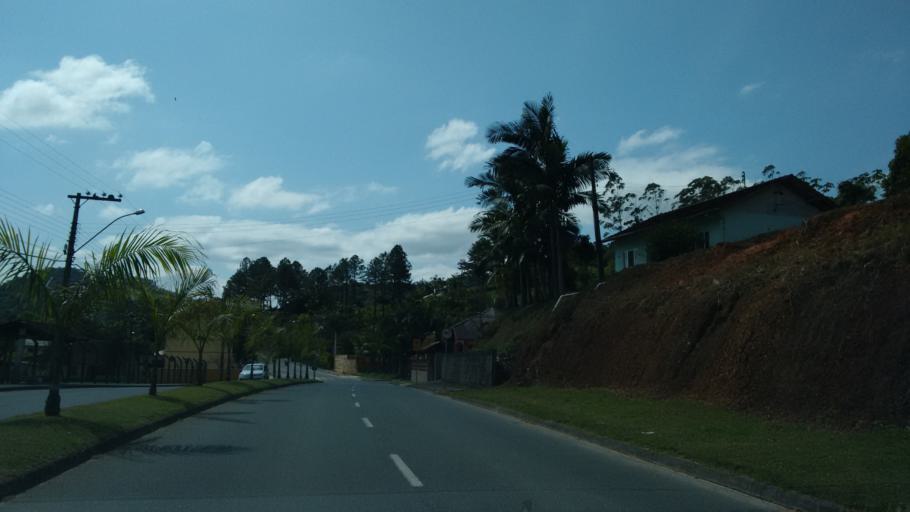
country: BR
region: Santa Catarina
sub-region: Pomerode
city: Pomerode
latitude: -26.7238
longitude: -49.1796
